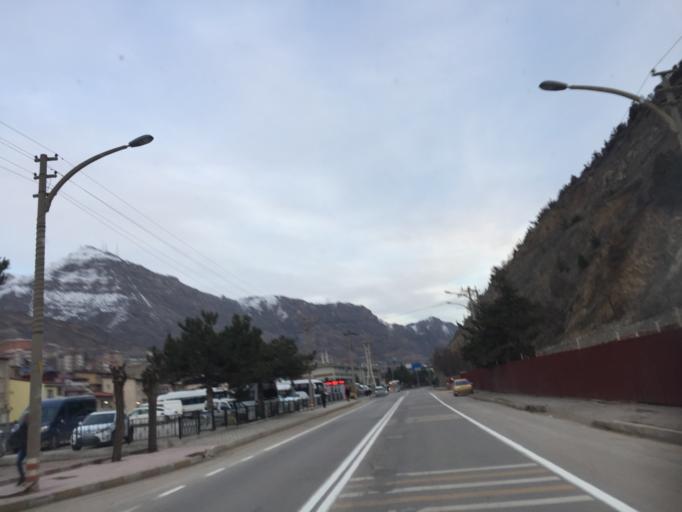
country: TR
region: Gumushane
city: Gumushkhane
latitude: 40.4609
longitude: 39.4709
